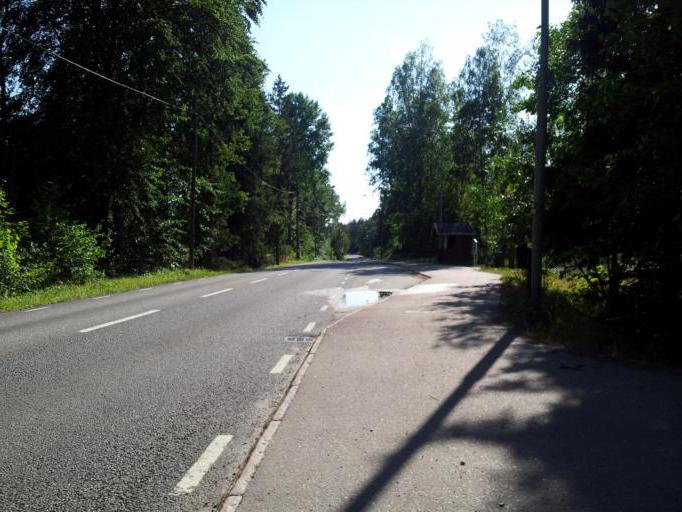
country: SE
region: Uppsala
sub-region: Knivsta Kommun
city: Knivsta
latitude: 59.8667
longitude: 17.9426
